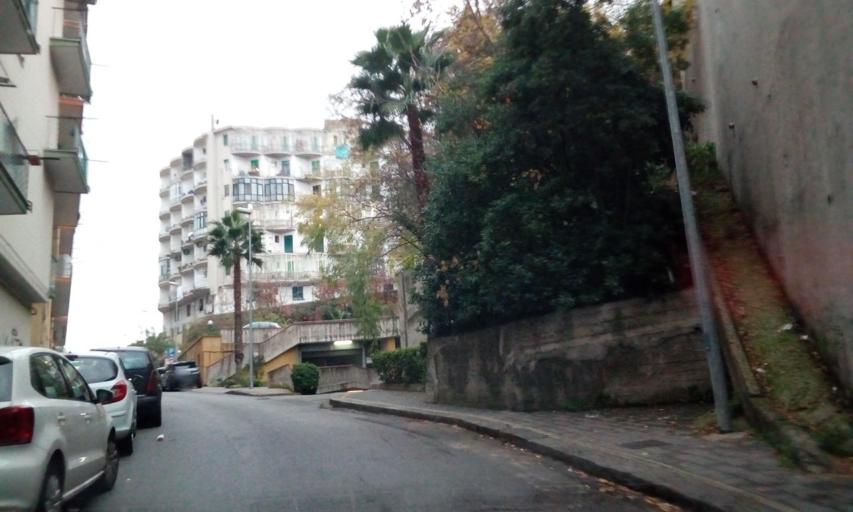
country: IT
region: Campania
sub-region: Provincia di Salerno
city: Capezzano Inferiore
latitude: 40.6866
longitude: 14.7702
